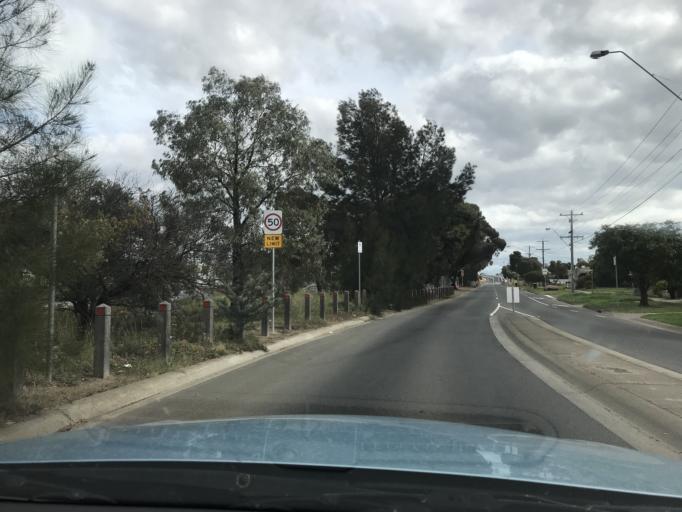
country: AU
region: Victoria
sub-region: Hobsons Bay
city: Laverton
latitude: -37.8640
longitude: 144.7694
